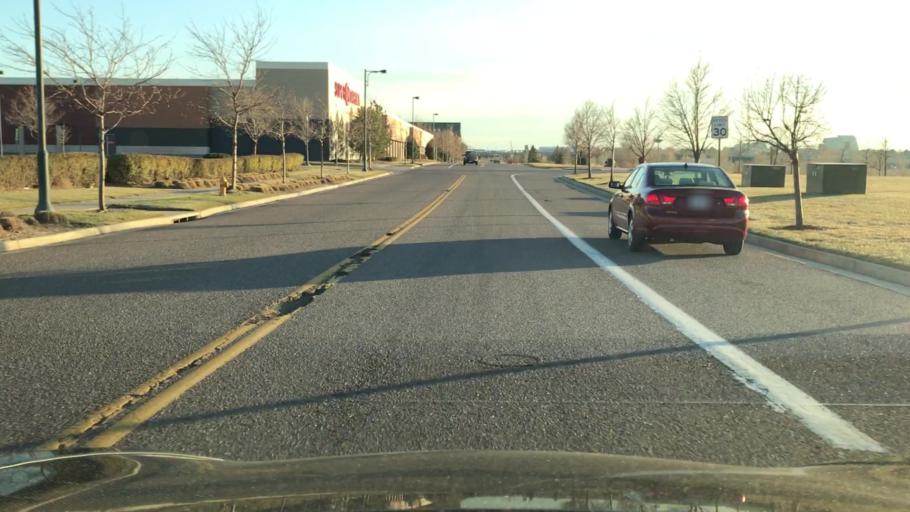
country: US
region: Colorado
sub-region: Adams County
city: Commerce City
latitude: 39.7852
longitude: -104.8963
